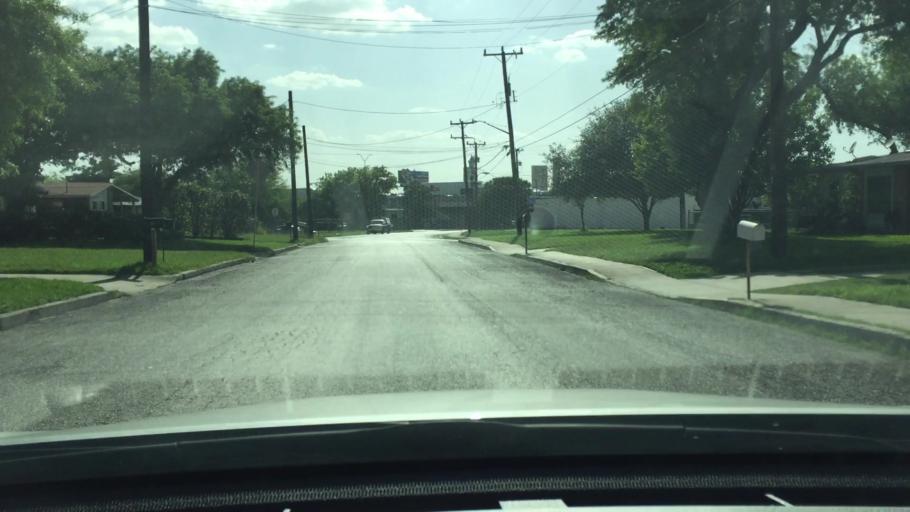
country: US
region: Texas
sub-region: Bexar County
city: Windcrest
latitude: 29.5327
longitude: -98.3873
